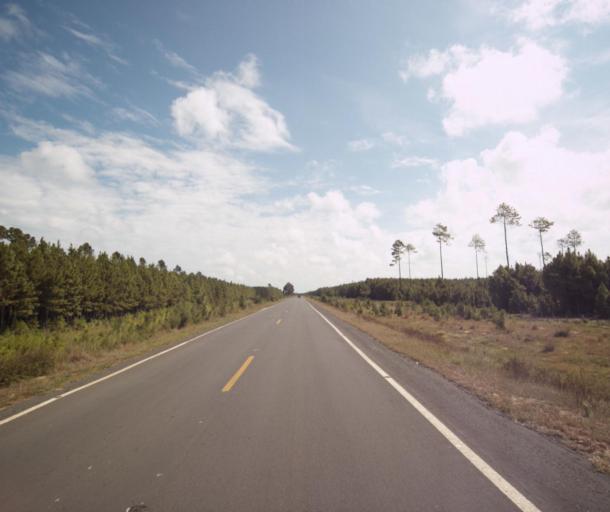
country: BR
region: Rio Grande do Sul
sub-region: Sao Lourenco Do Sul
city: Sao Lourenco do Sul
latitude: -31.4474
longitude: -51.2079
